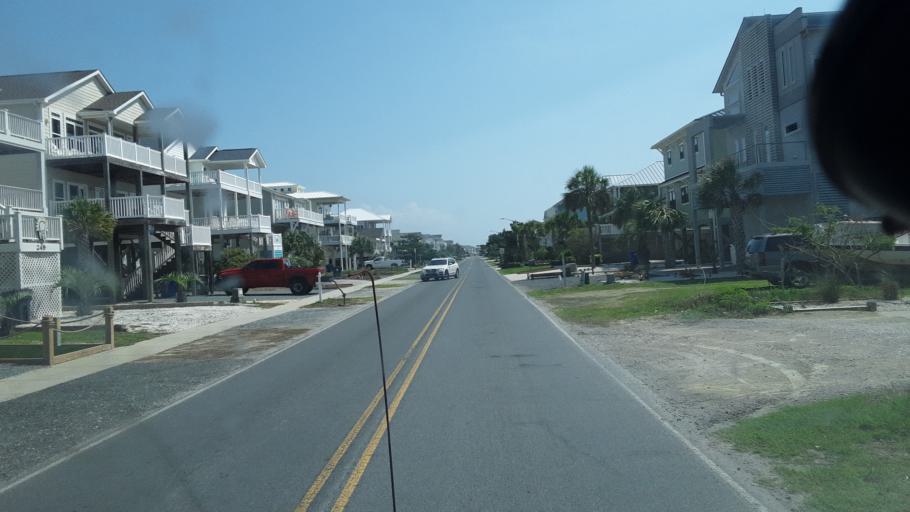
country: US
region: North Carolina
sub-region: Brunswick County
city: Shallotte
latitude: 33.8930
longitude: -78.4152
